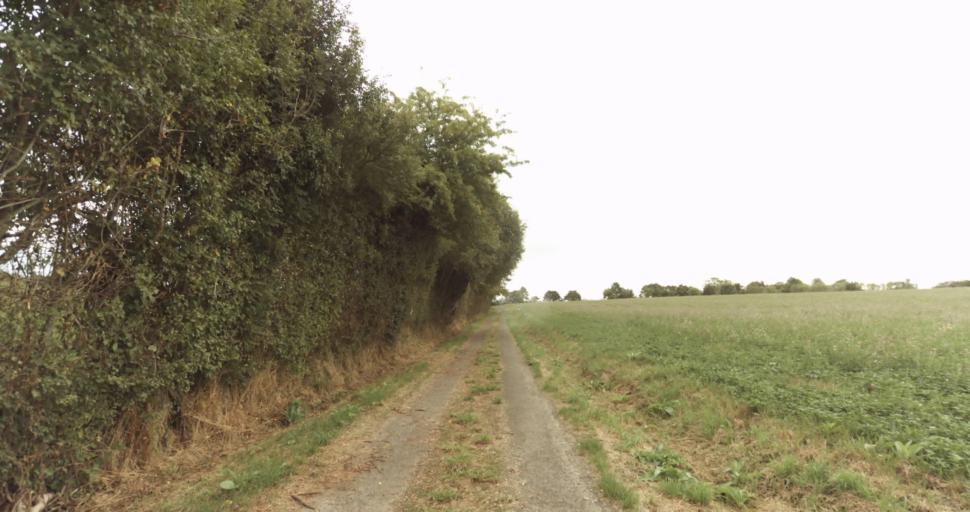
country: FR
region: Lower Normandy
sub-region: Departement de l'Orne
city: Sees
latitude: 48.6747
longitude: 0.2334
